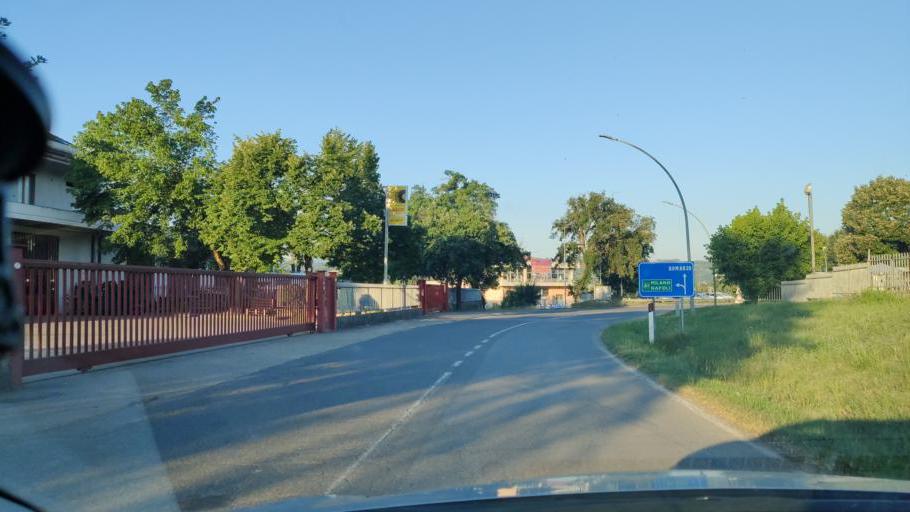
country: IT
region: Umbria
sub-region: Provincia di Terni
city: Attigliano
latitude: 42.5106
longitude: 12.2992
